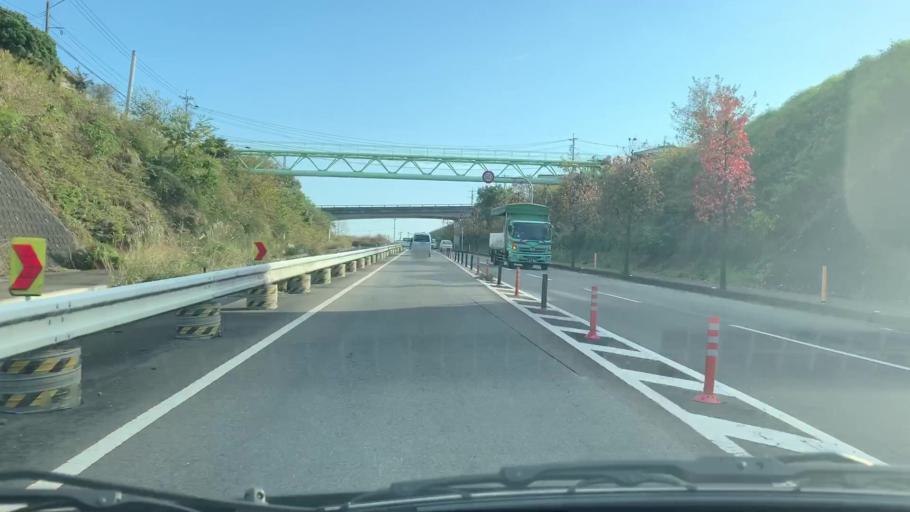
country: JP
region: Saga Prefecture
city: Kashima
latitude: 33.1019
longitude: 130.0868
